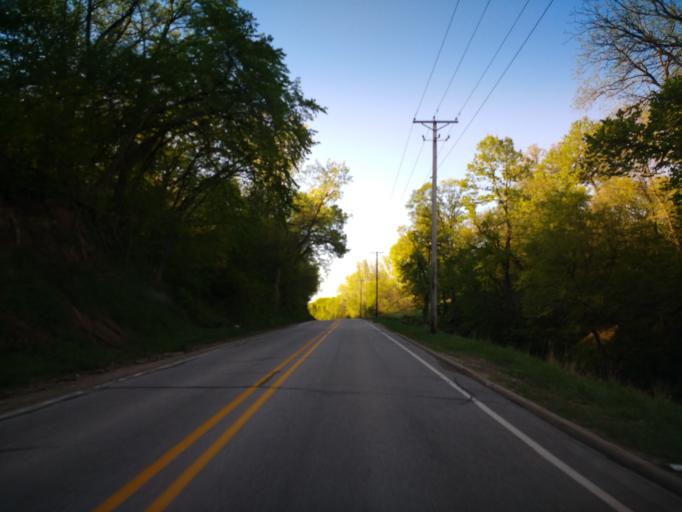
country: US
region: Iowa
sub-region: Harrison County
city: Missouri Valley
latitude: 41.4228
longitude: -95.8517
